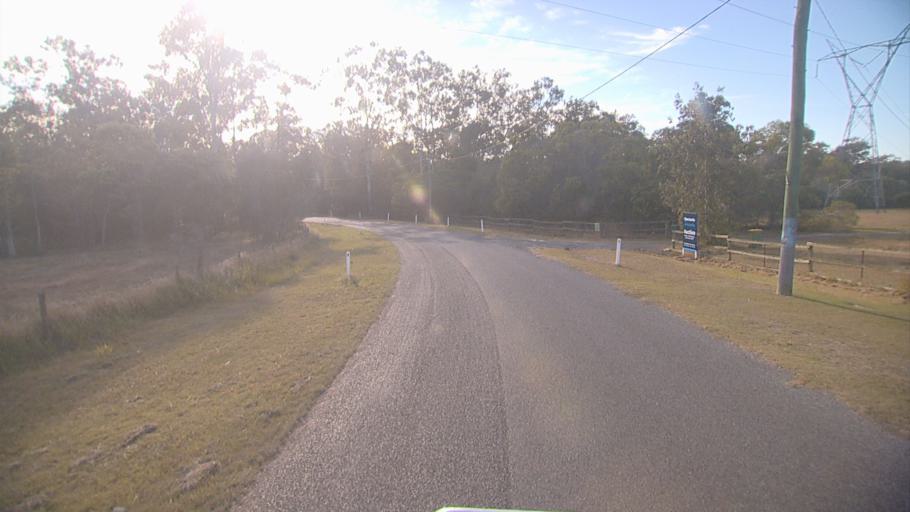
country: AU
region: Queensland
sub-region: Logan
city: North Maclean
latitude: -27.7573
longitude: 153.0057
